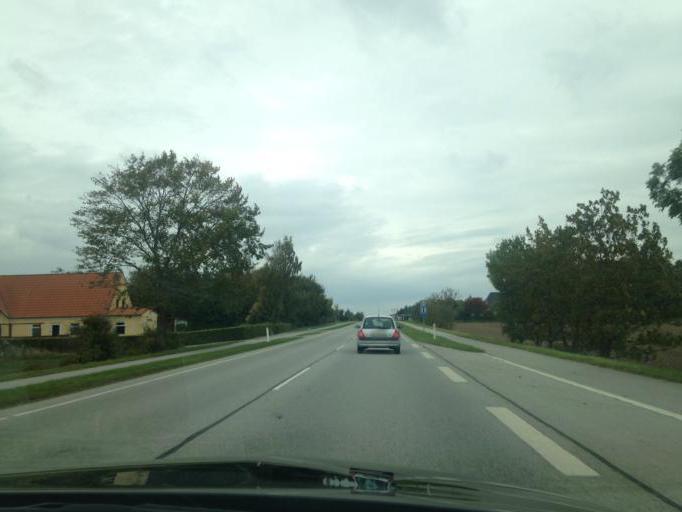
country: DK
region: South Denmark
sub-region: Kolding Kommune
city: Christiansfeld
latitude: 55.3211
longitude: 9.4951
